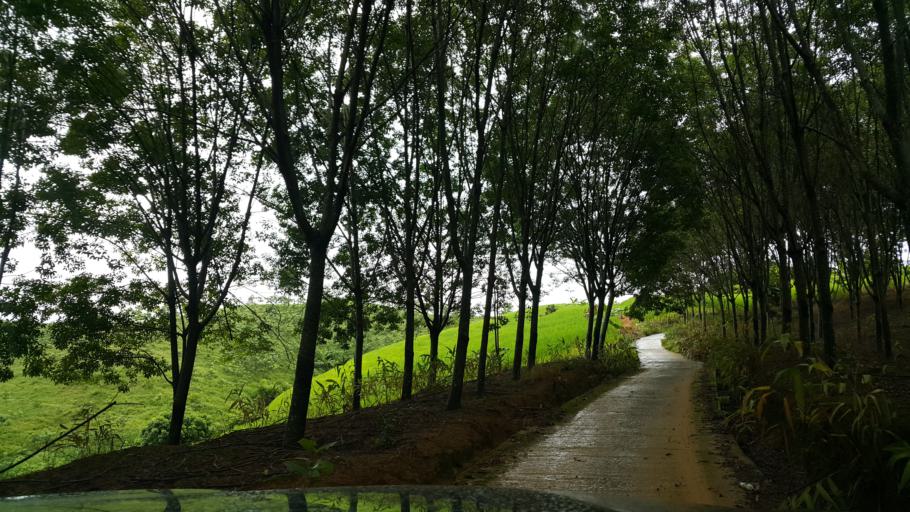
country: TH
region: Phayao
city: Chiang Kham
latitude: 19.4986
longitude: 100.4648
